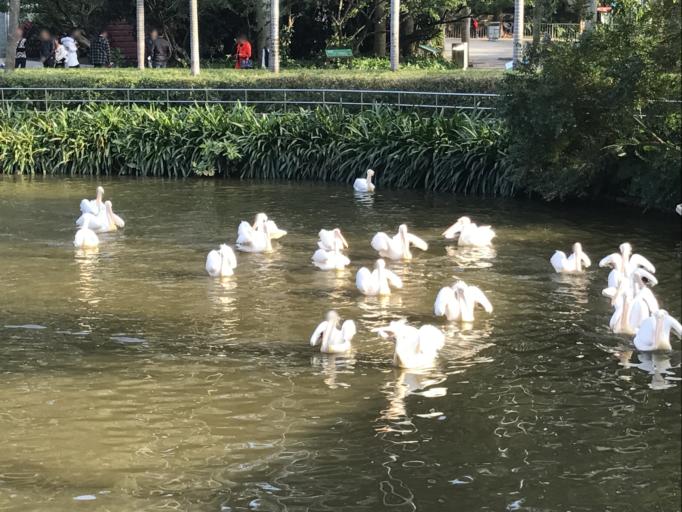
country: CN
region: Guangdong
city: Wushan
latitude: 23.1431
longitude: 113.2988
